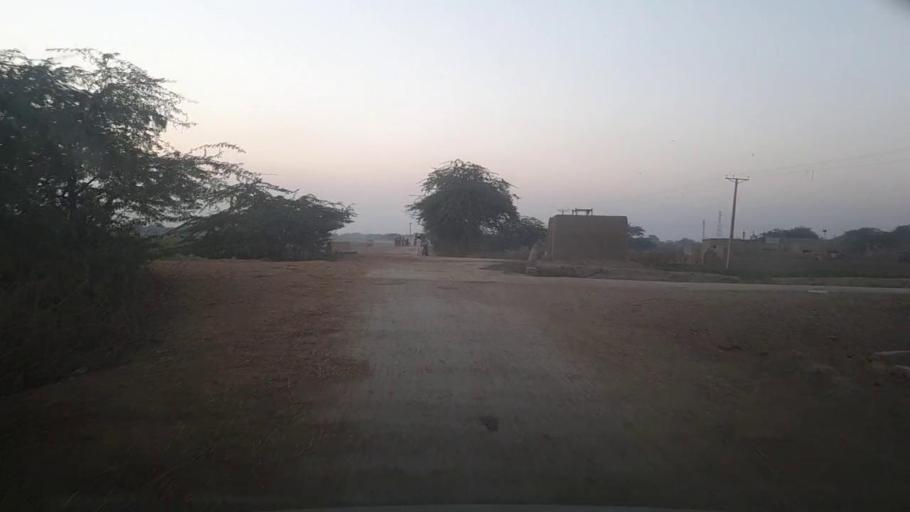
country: PK
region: Sindh
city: Khairpur Nathan Shah
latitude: 27.1820
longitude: 67.5991
